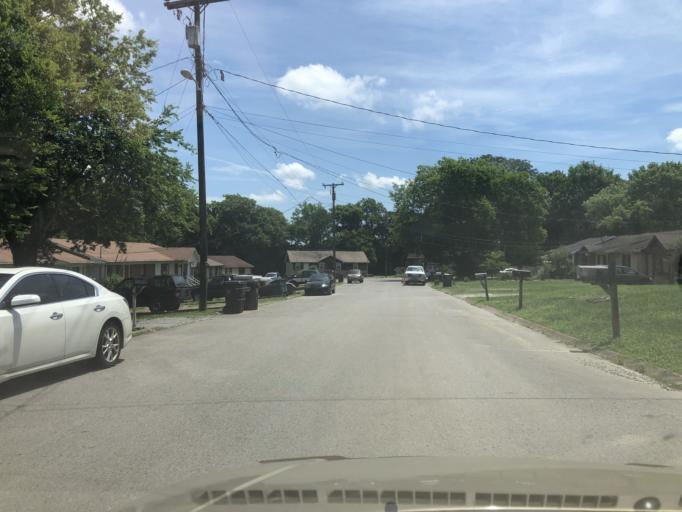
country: US
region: Tennessee
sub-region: Davidson County
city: Lakewood
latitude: 36.2485
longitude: -86.6782
